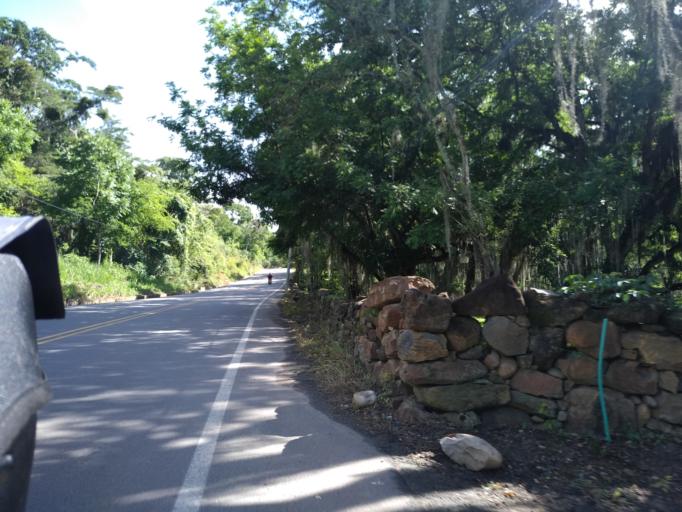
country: CO
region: Santander
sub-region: San Gil
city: San Gil
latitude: 6.5232
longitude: -73.1253
